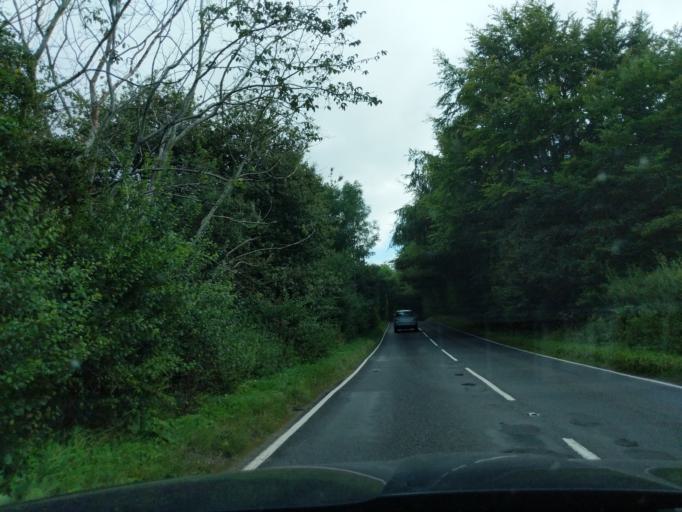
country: GB
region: England
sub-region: Northumberland
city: Ford
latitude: 55.5798
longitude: -2.0882
